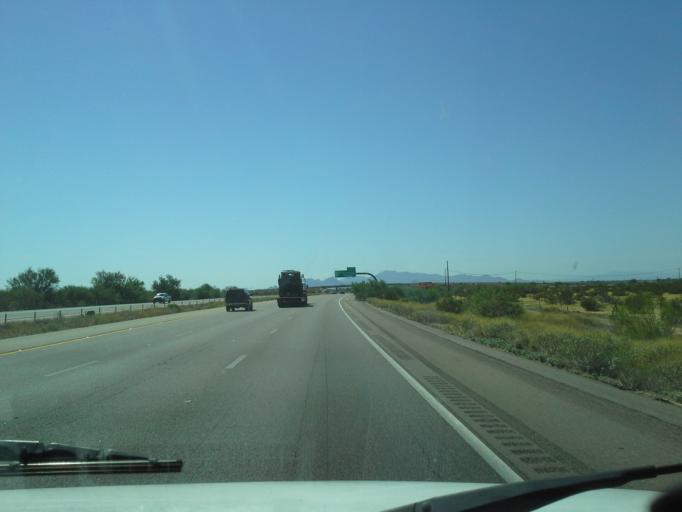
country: US
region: Arizona
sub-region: Pima County
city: Avra Valley
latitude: 32.5122
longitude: -111.2723
